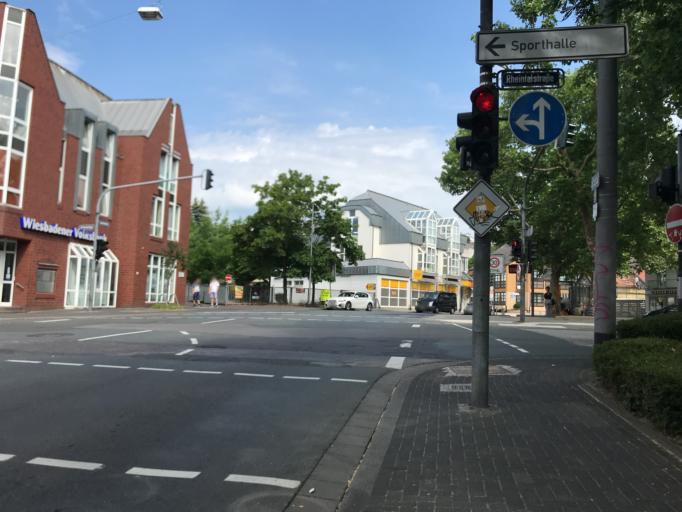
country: DE
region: Hesse
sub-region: Regierungsbezirk Darmstadt
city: Walluf
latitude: 50.0724
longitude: 8.1949
